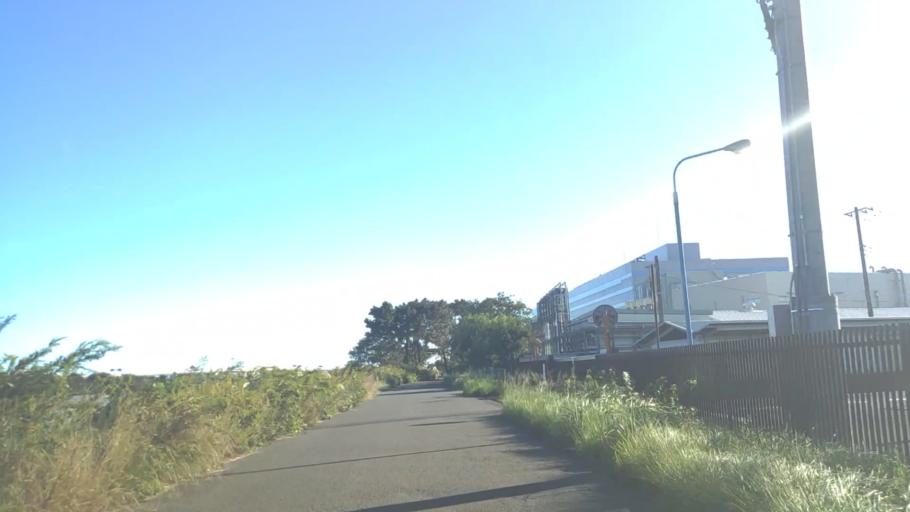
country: JP
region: Kanagawa
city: Atsugi
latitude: 35.4304
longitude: 139.3712
